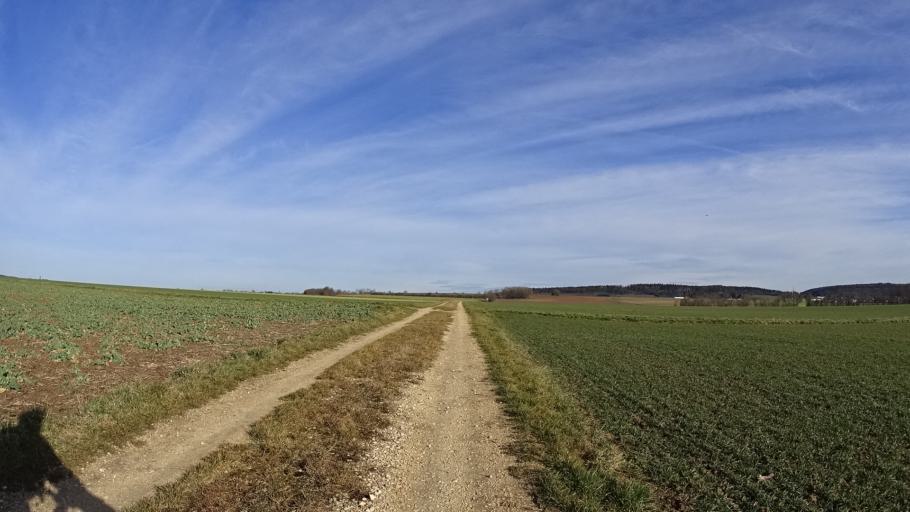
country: DE
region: Bavaria
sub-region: Upper Bavaria
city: Eitensheim
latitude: 48.8276
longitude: 11.3414
